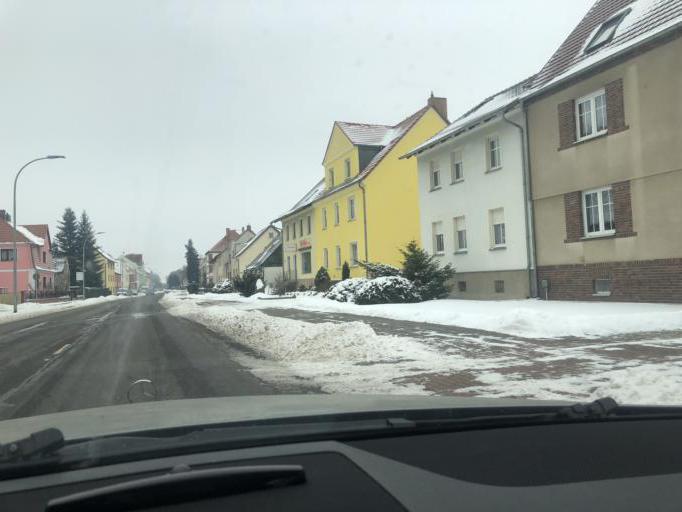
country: DE
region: Brandenburg
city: Guben
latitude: 51.9645
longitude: 14.7020
